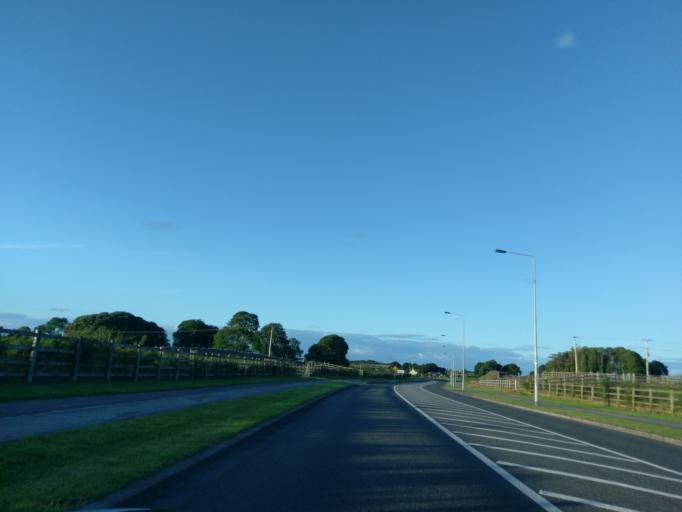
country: IE
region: Connaught
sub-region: County Galway
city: Athenry
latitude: 53.3091
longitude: -8.7585
